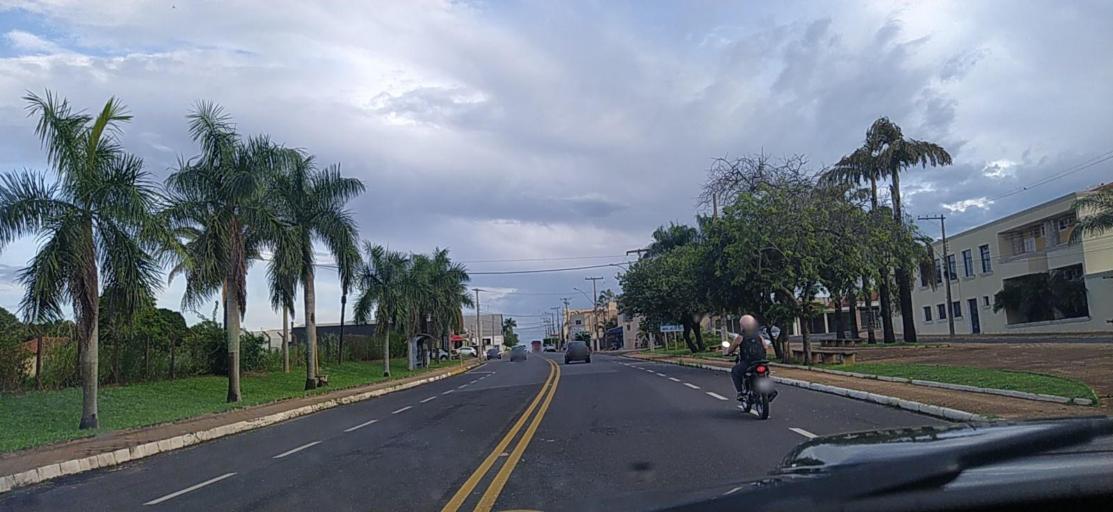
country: BR
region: Sao Paulo
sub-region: Pindorama
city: Pindorama
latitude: -21.1829
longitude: -48.9141
